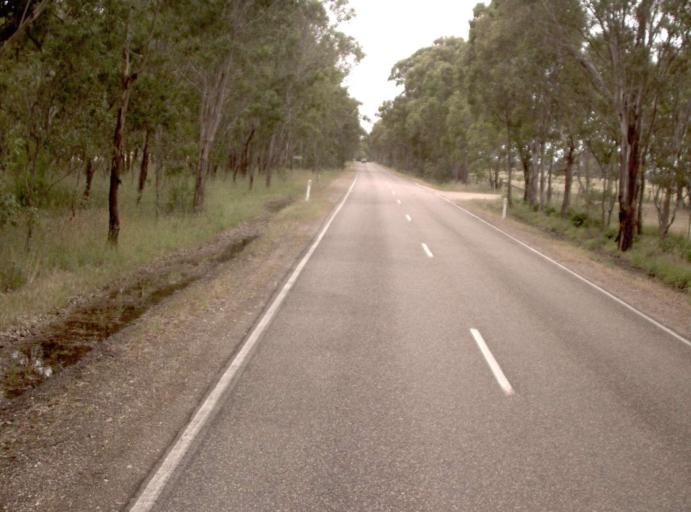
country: AU
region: Victoria
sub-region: Wellington
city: Sale
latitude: -37.9590
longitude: 147.0997
